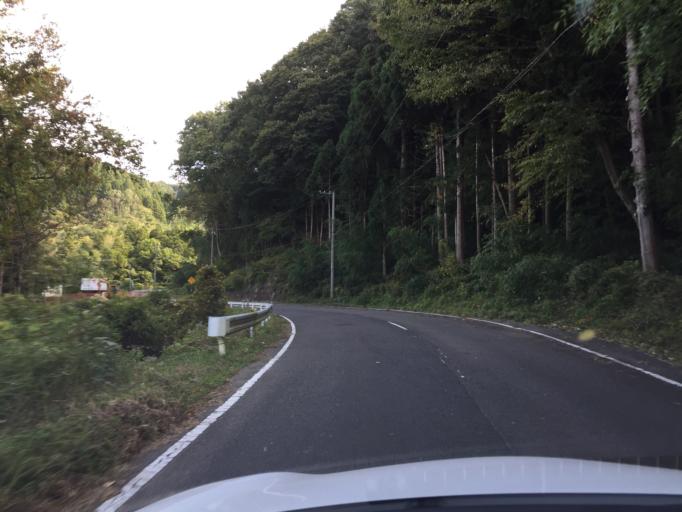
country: JP
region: Fukushima
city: Miharu
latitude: 37.3900
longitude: 140.4532
